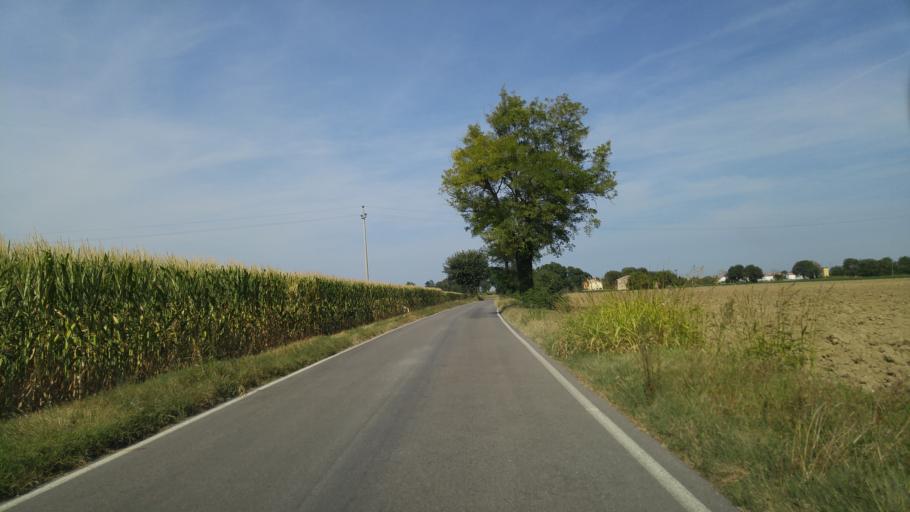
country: IT
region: The Marches
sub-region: Provincia di Pesaro e Urbino
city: Cuccurano
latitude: 43.7933
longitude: 12.9804
